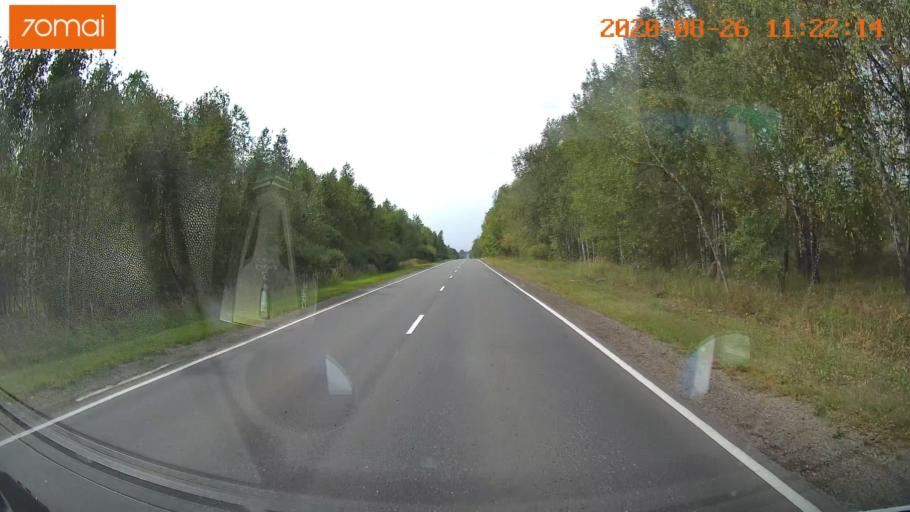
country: RU
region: Rjazan
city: Shilovo
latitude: 54.3665
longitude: 41.0308
